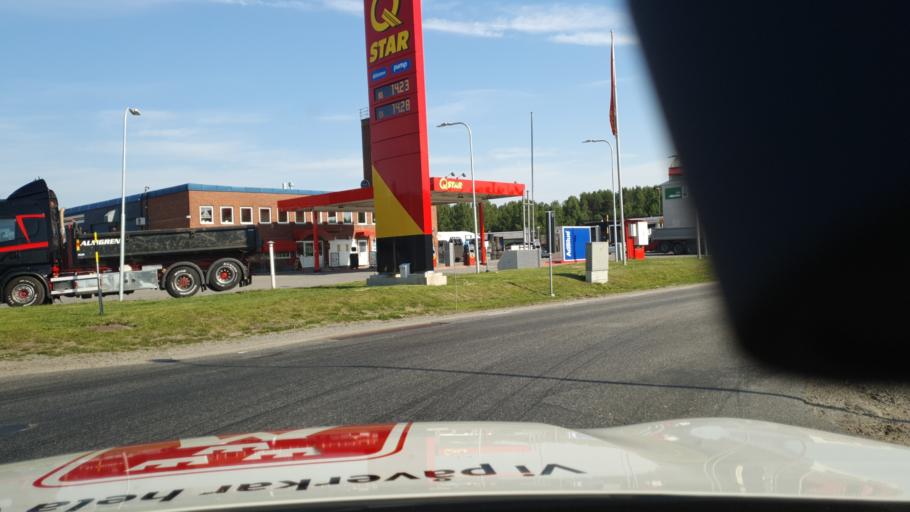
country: SE
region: Vaesterbotten
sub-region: Skelleftea Kommun
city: Soedra Bergsbyn
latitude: 64.7452
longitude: 21.0321
